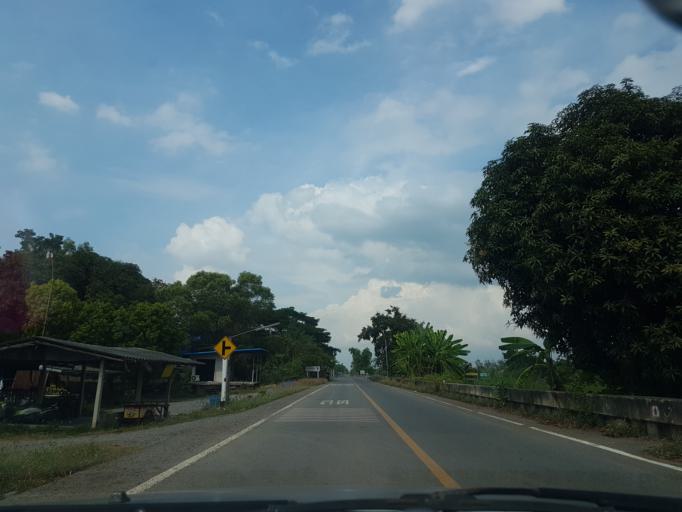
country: TH
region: Pathum Thani
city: Nong Suea
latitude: 14.2188
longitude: 100.8914
